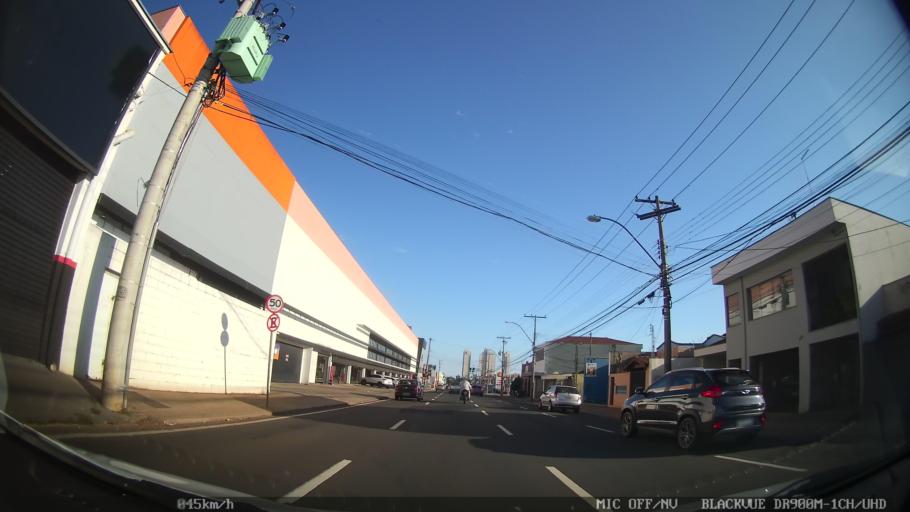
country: BR
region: Sao Paulo
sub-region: Piracicaba
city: Piracicaba
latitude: -22.7102
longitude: -47.6552
